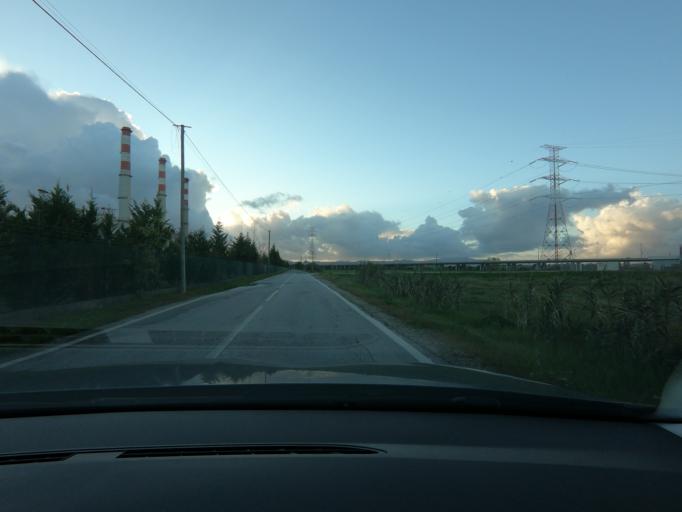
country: PT
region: Lisbon
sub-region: Alenquer
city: Carregado
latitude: 39.0130
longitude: -8.9519
